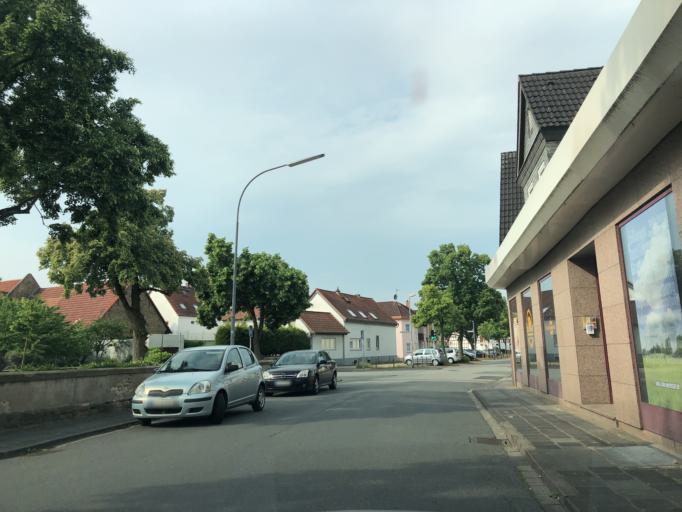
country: DE
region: Hesse
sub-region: Regierungsbezirk Darmstadt
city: Nauheim
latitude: 49.9643
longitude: 8.4519
